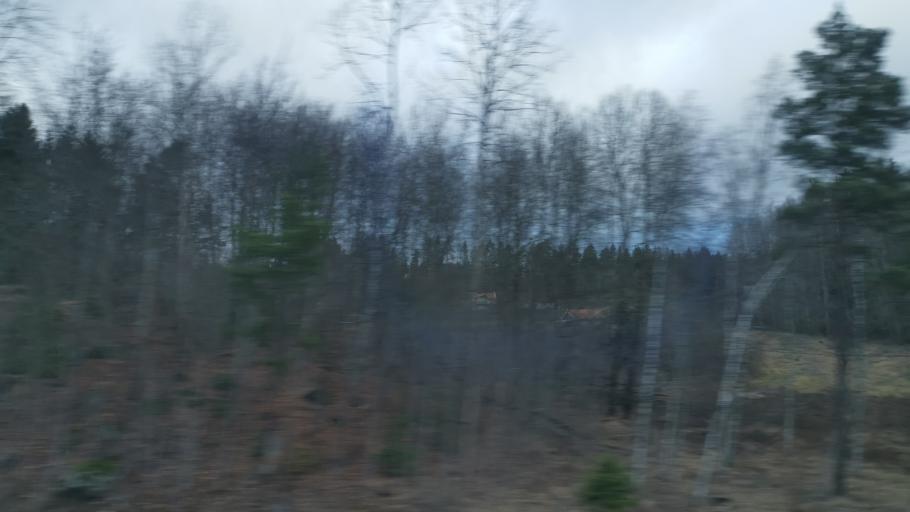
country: SE
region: Stockholm
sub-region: Sodertalje Kommun
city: Molnbo
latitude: 59.0500
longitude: 17.4312
